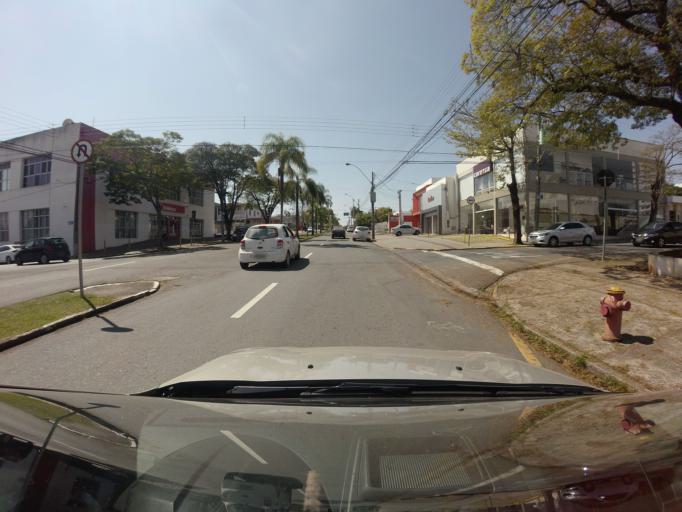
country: BR
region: Sao Paulo
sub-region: Piracicaba
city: Piracicaba
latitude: -22.7173
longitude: -47.6390
